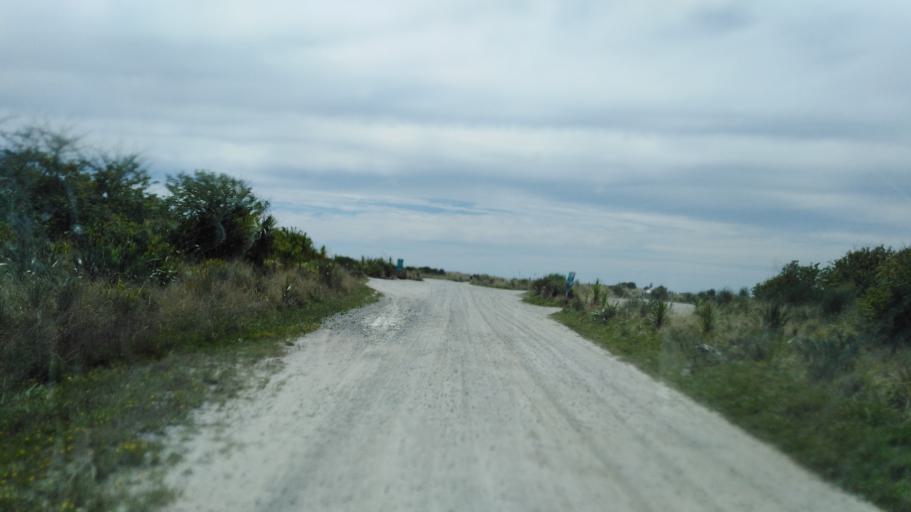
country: NZ
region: West Coast
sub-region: Buller District
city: Westport
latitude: -41.7352
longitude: 171.6055
